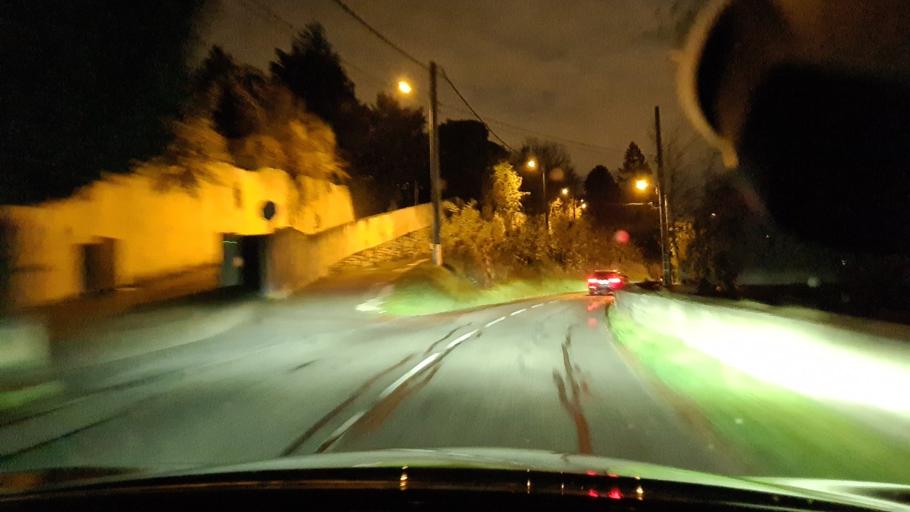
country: FR
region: Rhone-Alpes
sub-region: Departement du Rhone
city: Limonest
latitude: 45.8228
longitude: 4.7904
